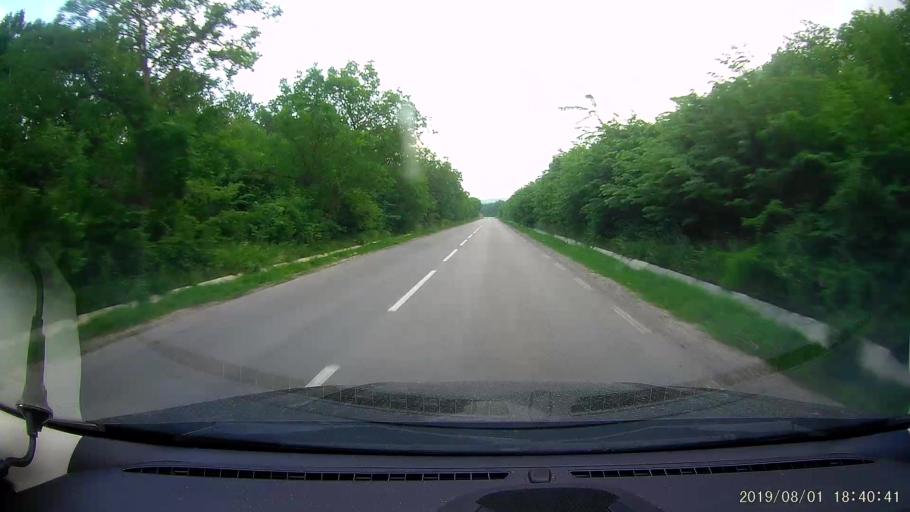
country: BG
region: Shumen
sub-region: Obshtina Khitrino
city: Gara Khitrino
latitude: 43.3613
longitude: 26.9203
